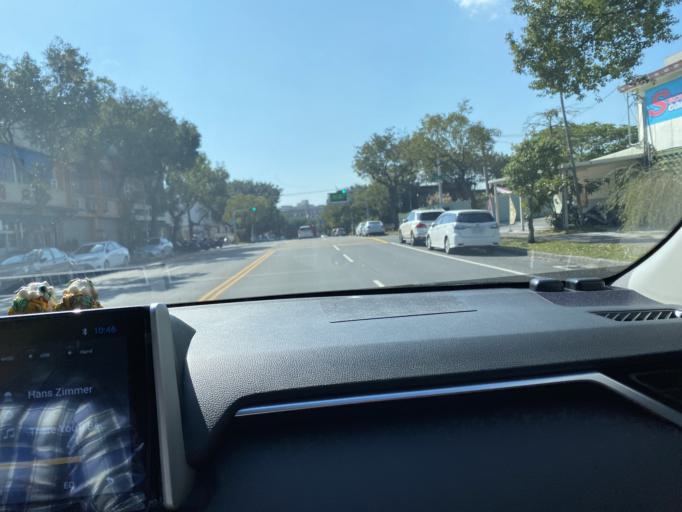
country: TW
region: Taiwan
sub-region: Hualien
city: Hualian
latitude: 23.9881
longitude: 121.6212
